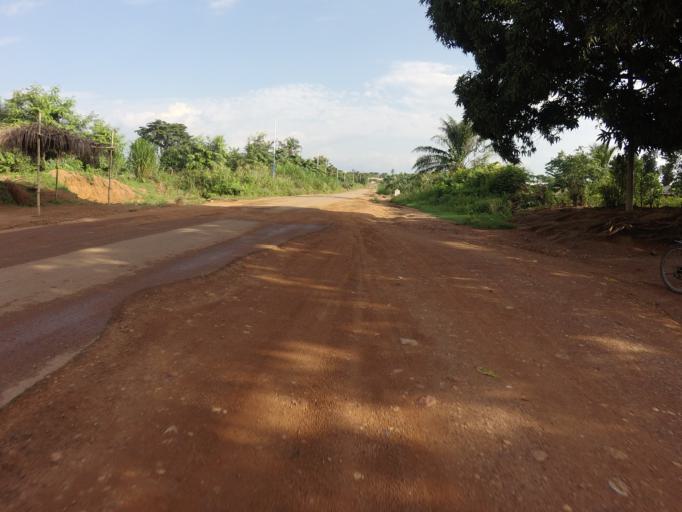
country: GH
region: Volta
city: Hohoe
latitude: 7.1204
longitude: 0.4580
